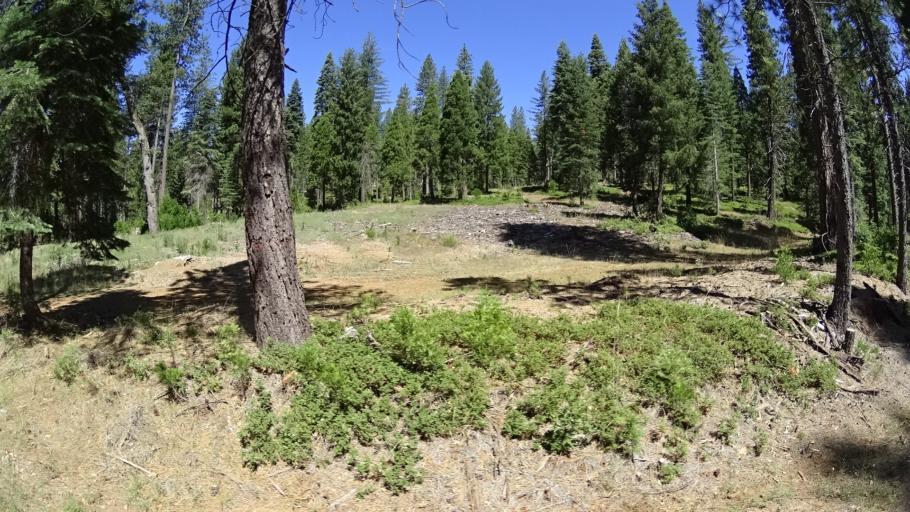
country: US
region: California
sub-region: Amador County
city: Pioneer
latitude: 38.4360
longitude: -120.4366
